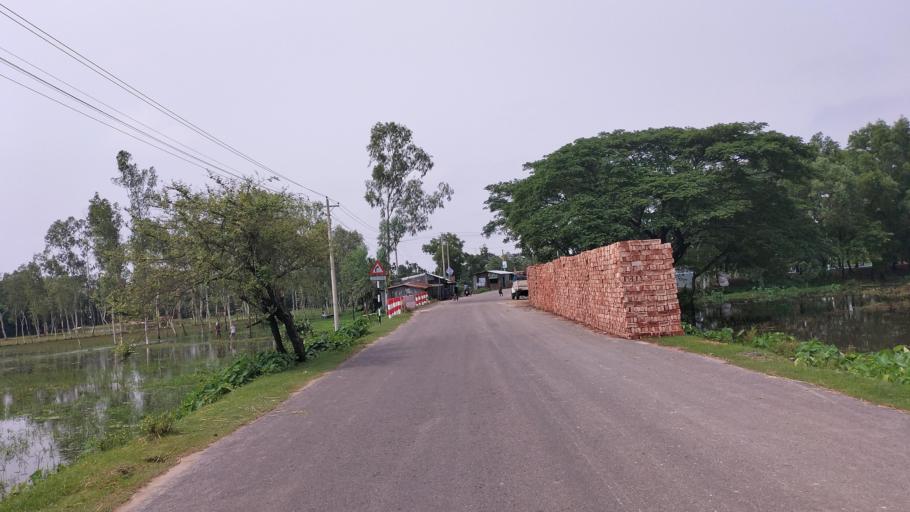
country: BD
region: Dhaka
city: Netrakona
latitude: 24.9509
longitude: 90.8328
